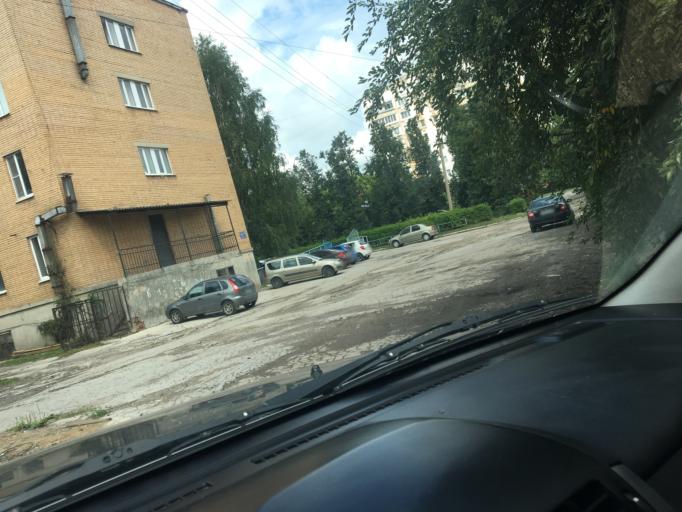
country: RU
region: Tula
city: Mendeleyevskiy
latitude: 54.1548
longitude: 37.5957
